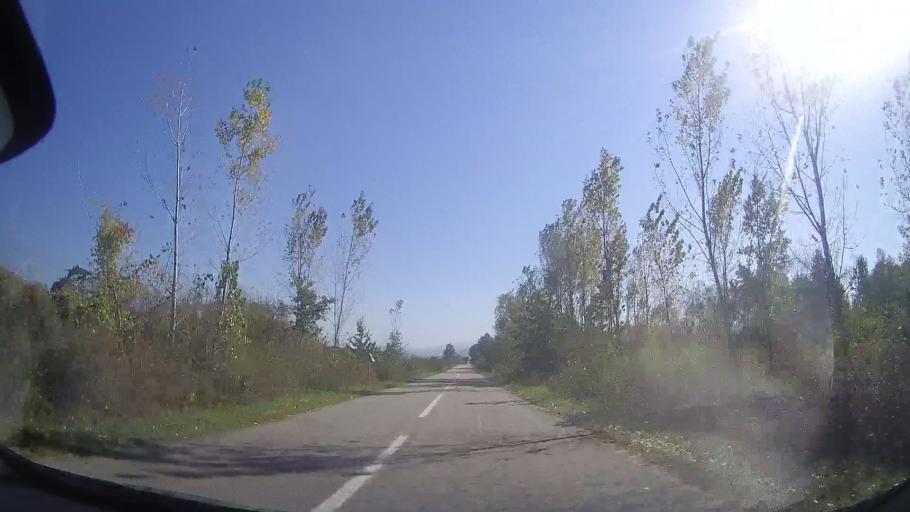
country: RO
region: Timis
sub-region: Comuna Traian Vuia
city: Traian Vuia
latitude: 45.7871
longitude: 22.0377
